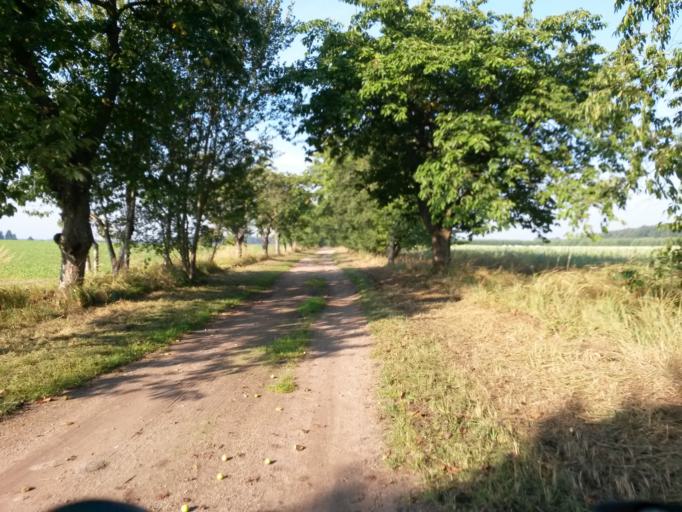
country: DE
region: Brandenburg
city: Templin
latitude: 53.1208
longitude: 13.4699
